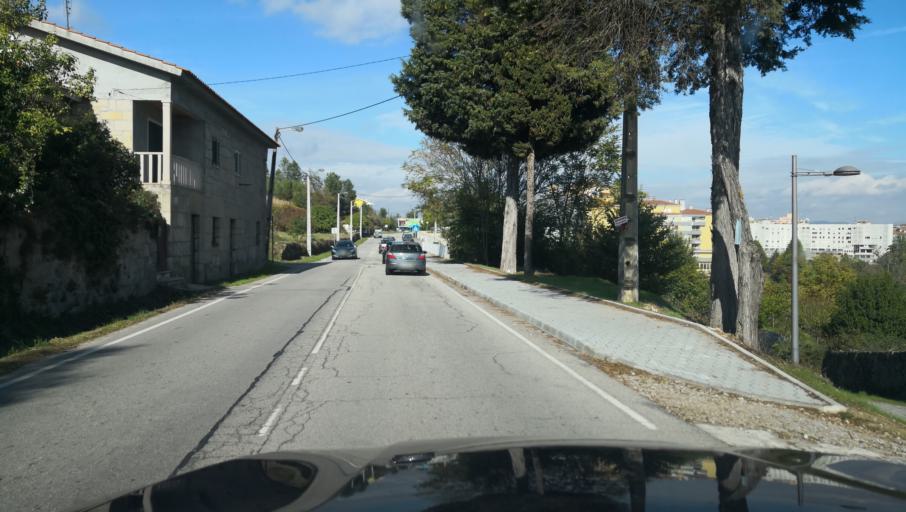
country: PT
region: Vila Real
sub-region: Chaves
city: Chaves
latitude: 41.7331
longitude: -7.4780
